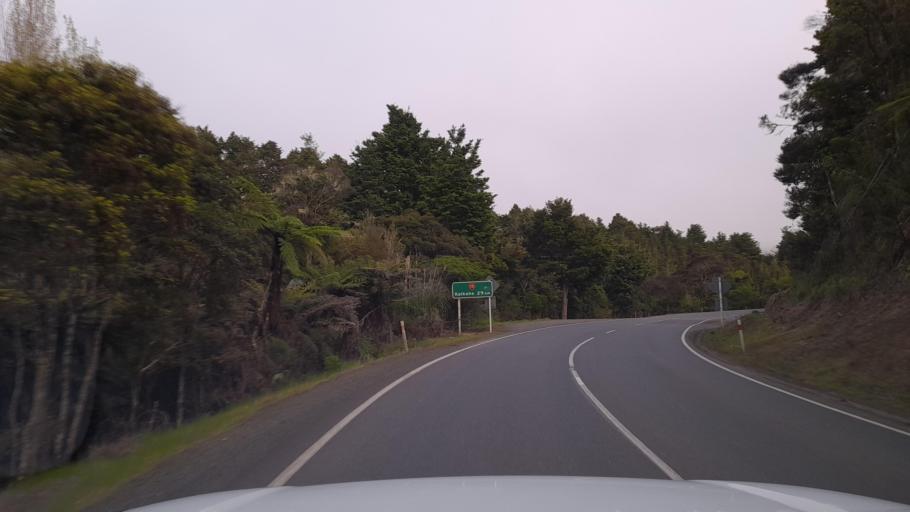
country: NZ
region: Northland
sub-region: Far North District
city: Moerewa
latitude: -35.6231
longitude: 173.8462
